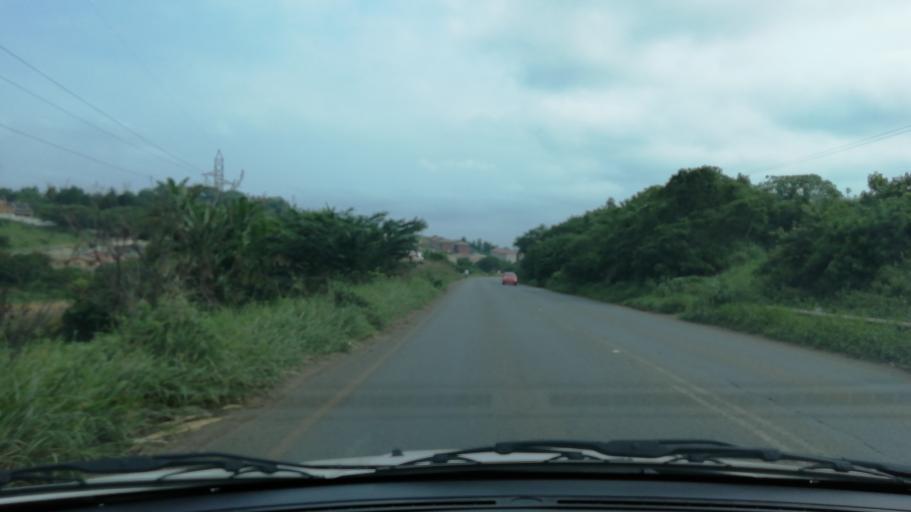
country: ZA
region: KwaZulu-Natal
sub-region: uThungulu District Municipality
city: Empangeni
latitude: -28.7462
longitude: 31.8807
